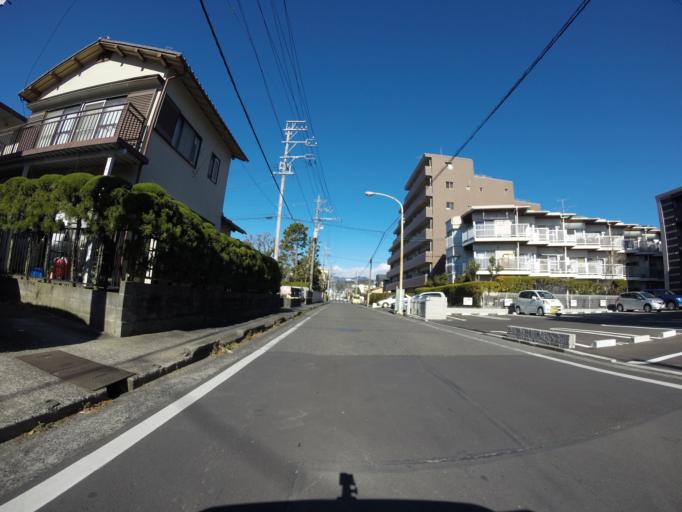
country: JP
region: Shizuoka
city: Shizuoka-shi
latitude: 34.9904
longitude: 138.3967
